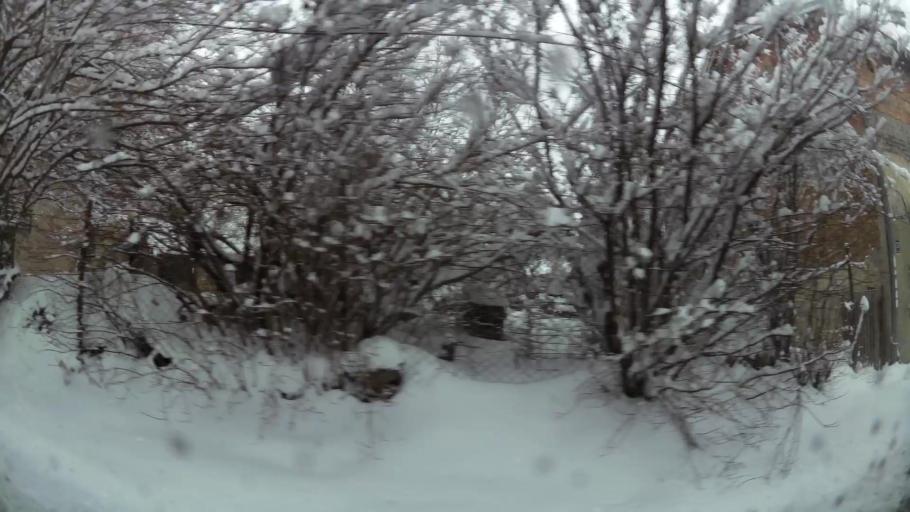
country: RS
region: Central Serbia
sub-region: Belgrade
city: Vracar
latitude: 44.7891
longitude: 20.4803
